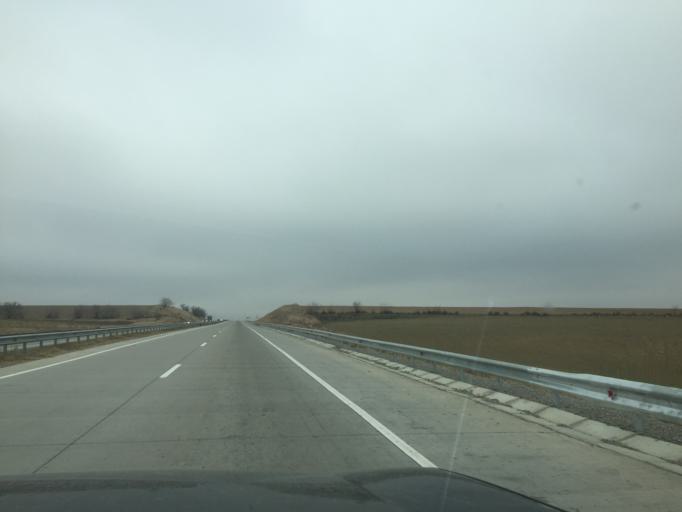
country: KZ
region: Ongtustik Qazaqstan
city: Aksu
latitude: 42.4754
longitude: 69.8903
